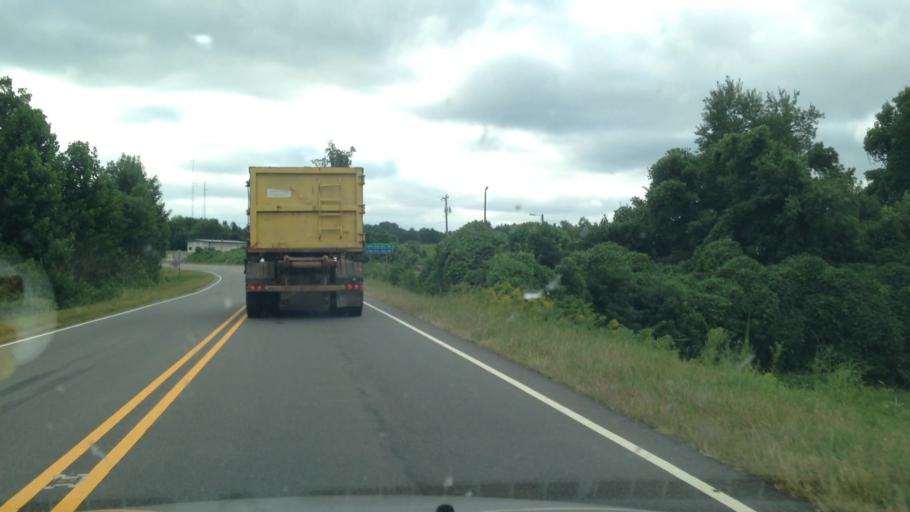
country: US
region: North Carolina
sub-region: Rockingham County
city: Wentworth
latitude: 36.3733
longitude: -79.7327
